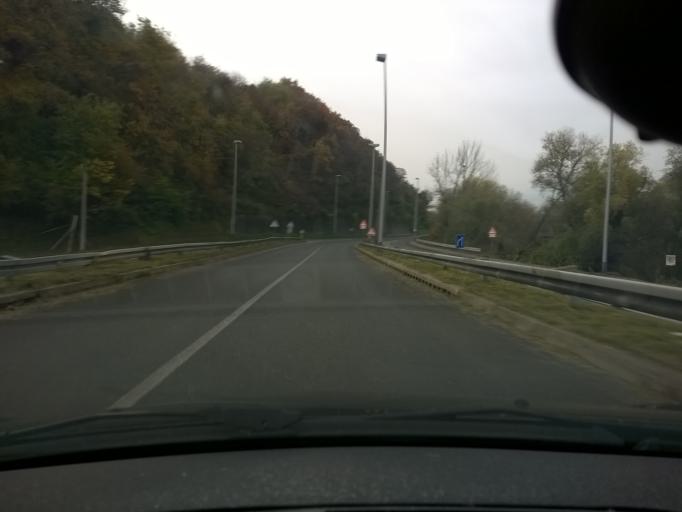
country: HR
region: Zagrebacka
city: Zapresic
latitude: 45.8365
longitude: 15.8245
